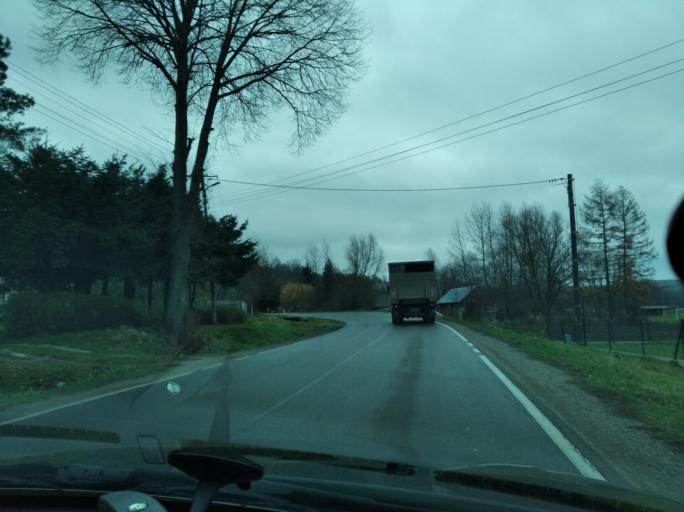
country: PL
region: Subcarpathian Voivodeship
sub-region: Powiat przeworski
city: Manasterz
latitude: 49.9361
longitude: 22.3512
